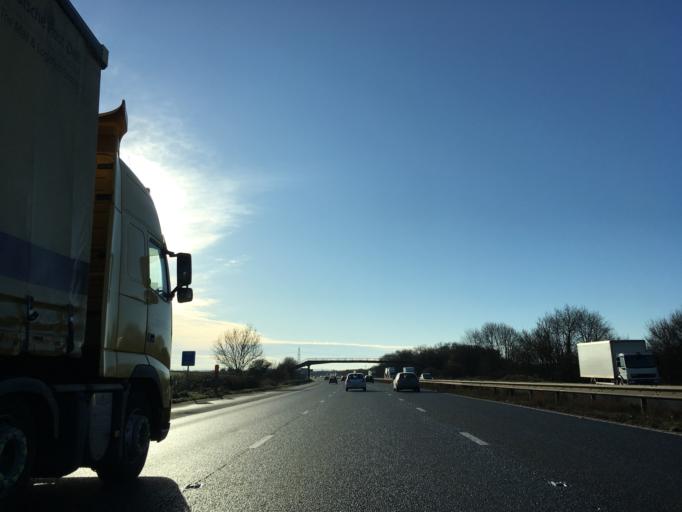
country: GB
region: England
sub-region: South Gloucestershire
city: Alveston
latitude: 51.5684
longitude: -2.5290
